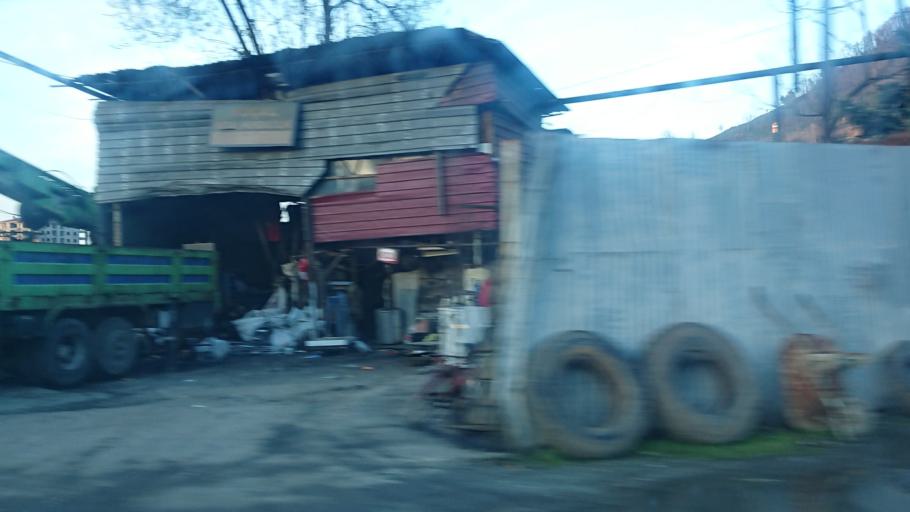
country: TR
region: Rize
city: Gundogdu
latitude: 41.0387
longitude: 40.5799
